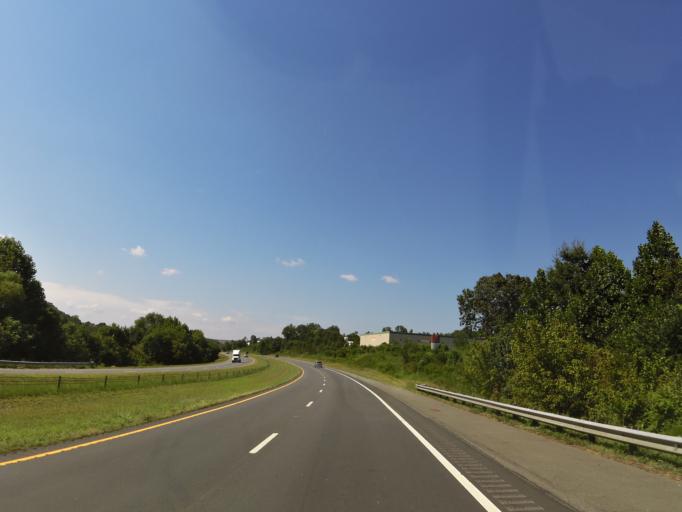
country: US
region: North Carolina
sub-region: Catawba County
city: Maiden
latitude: 35.5382
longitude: -81.2266
